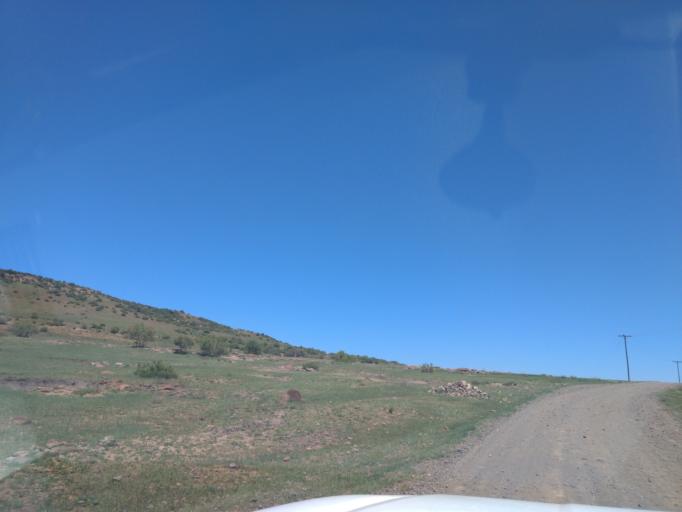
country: LS
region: Maseru
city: Maseru
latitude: -29.4662
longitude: 27.3759
